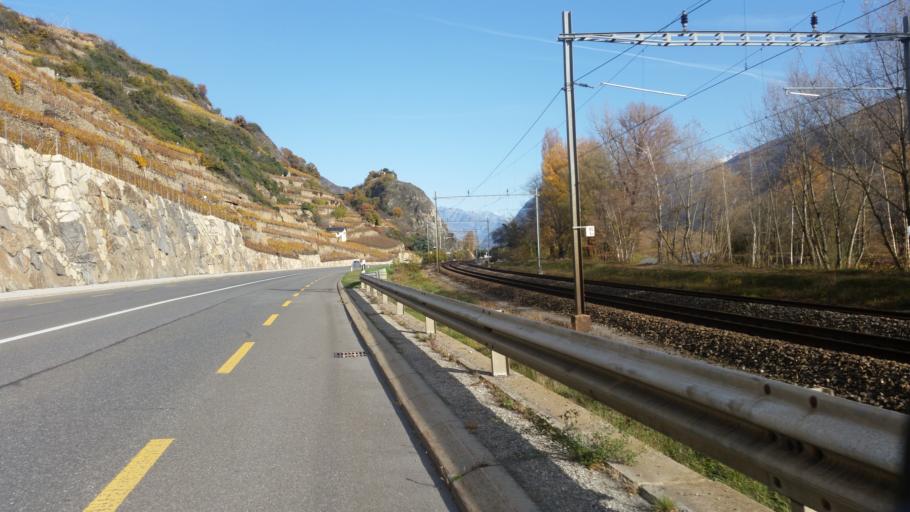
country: CH
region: Valais
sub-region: Sion District
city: Grimisuat
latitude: 46.2447
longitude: 7.3823
